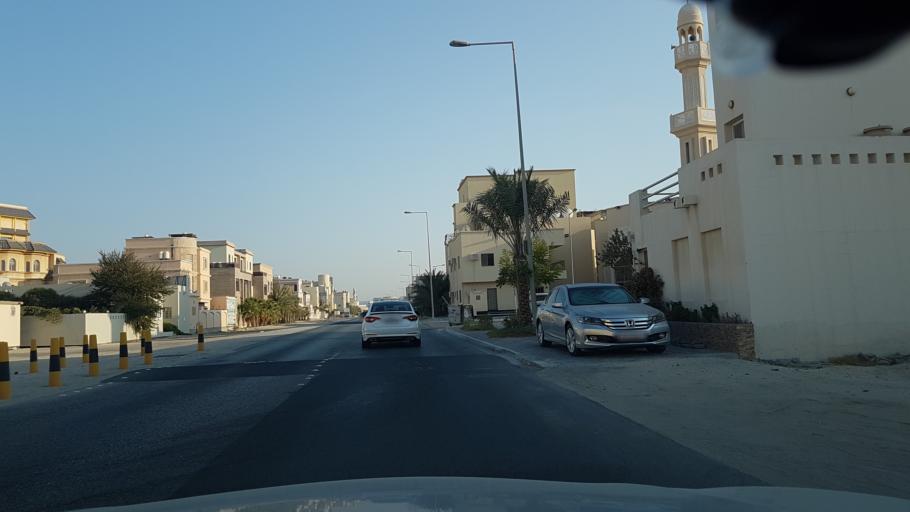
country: BH
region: Muharraq
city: Al Muharraq
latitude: 26.2772
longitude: 50.6030
